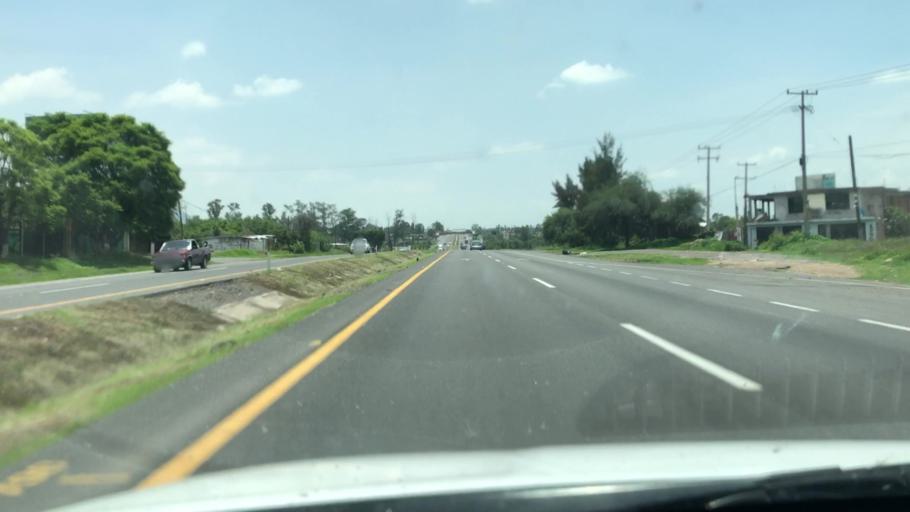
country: MX
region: Guanajuato
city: Penjamo
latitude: 20.4042
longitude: -101.7448
